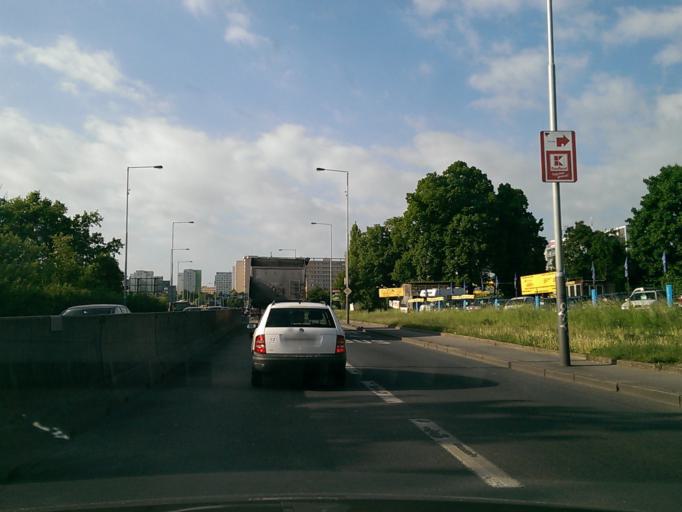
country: CZ
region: Praha
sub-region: Praha 4
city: Hodkovicky
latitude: 50.0322
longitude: 14.4550
